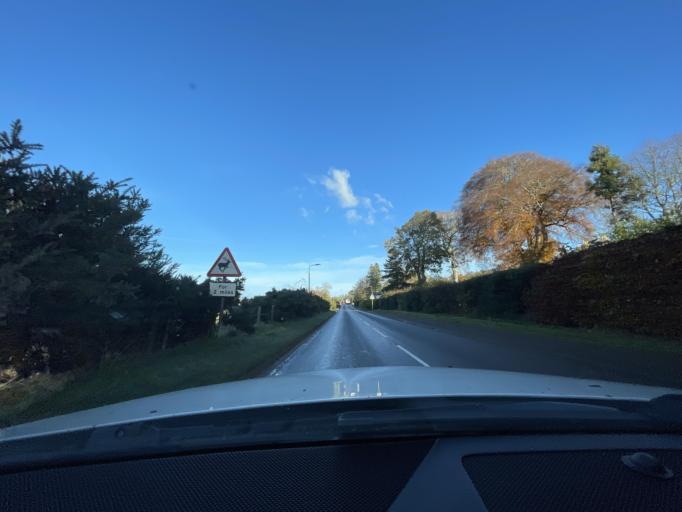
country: GB
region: Scotland
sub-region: Highland
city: Inverness
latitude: 57.3827
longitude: -4.3318
